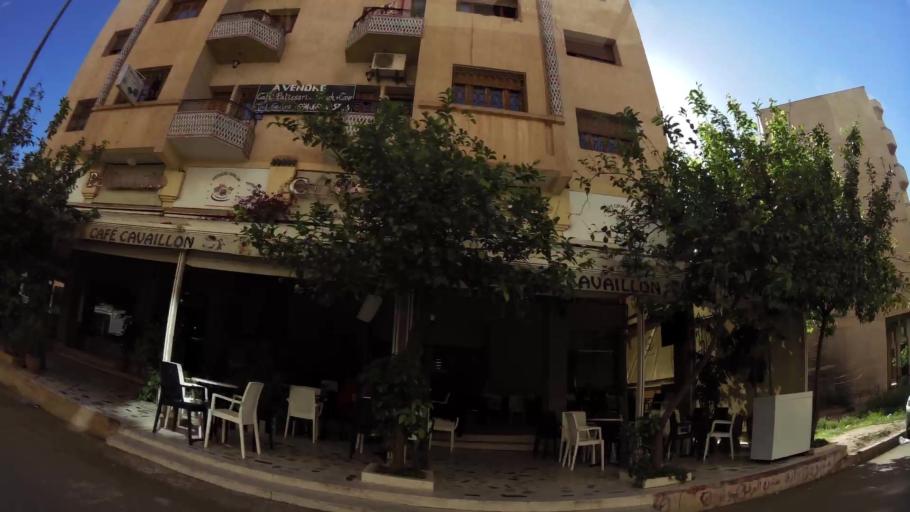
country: MA
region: Fes-Boulemane
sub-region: Fes
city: Fes
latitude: 34.0089
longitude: -4.9649
